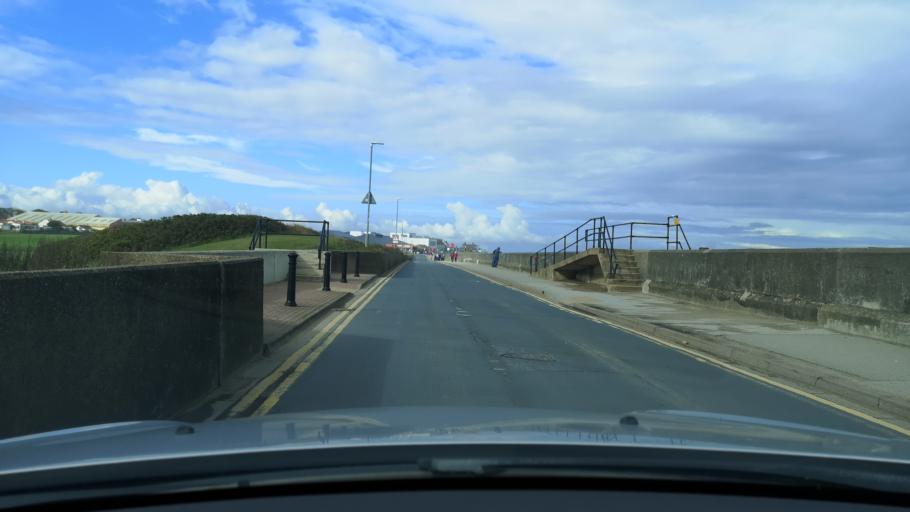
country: GB
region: England
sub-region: East Riding of Yorkshire
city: Hornsea
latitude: 53.9093
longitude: -0.1587
